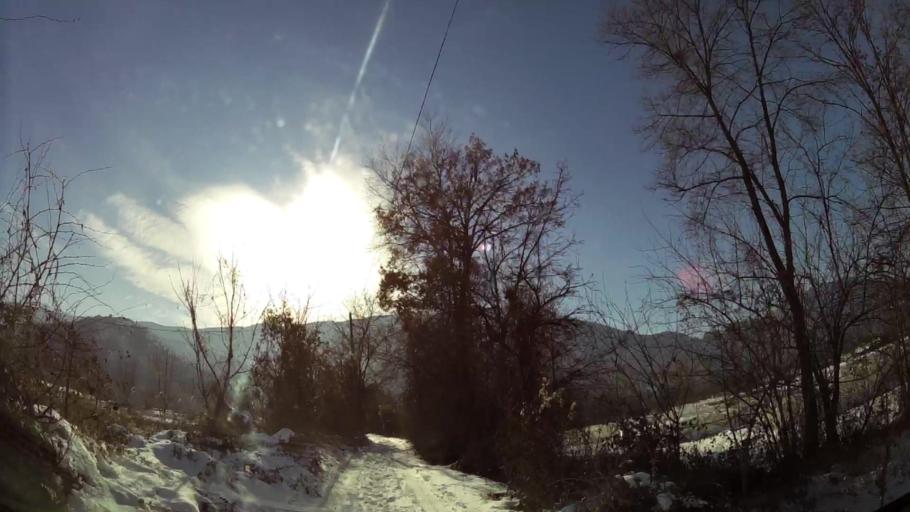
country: MK
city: Grchec
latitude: 41.9843
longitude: 21.3238
